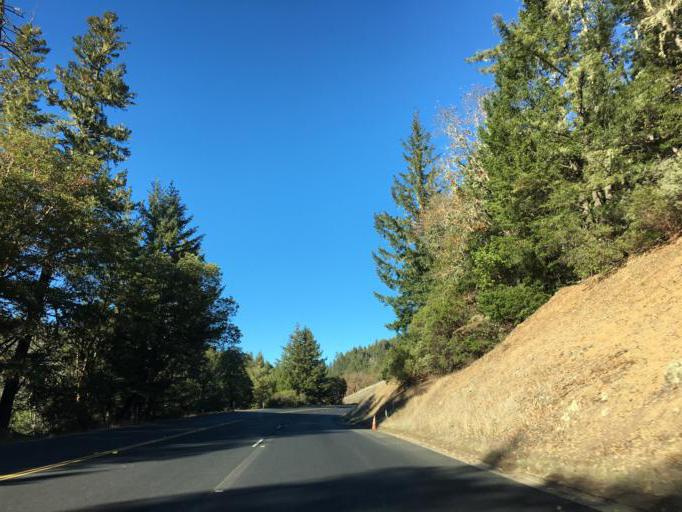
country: US
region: California
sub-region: Mendocino County
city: Laytonville
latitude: 39.7788
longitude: -123.5437
